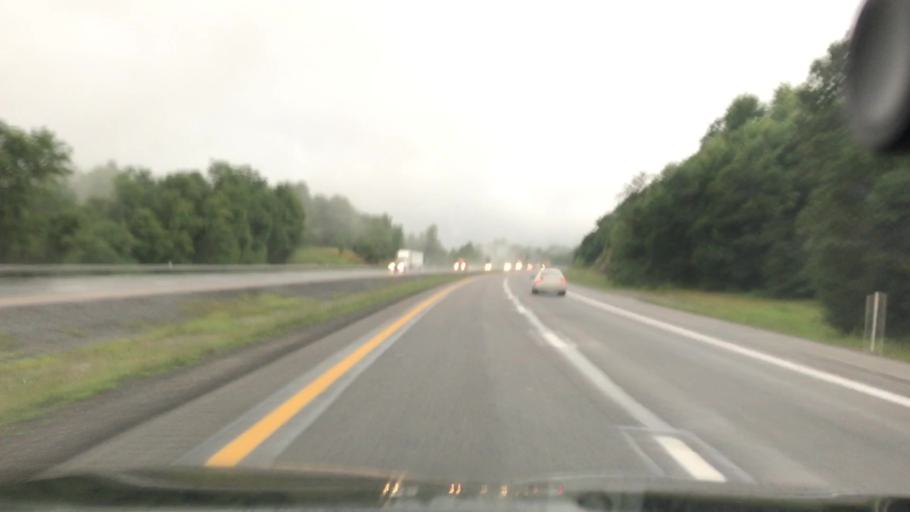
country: US
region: West Virginia
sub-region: Raleigh County
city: Shady Spring
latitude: 37.5777
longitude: -81.1159
